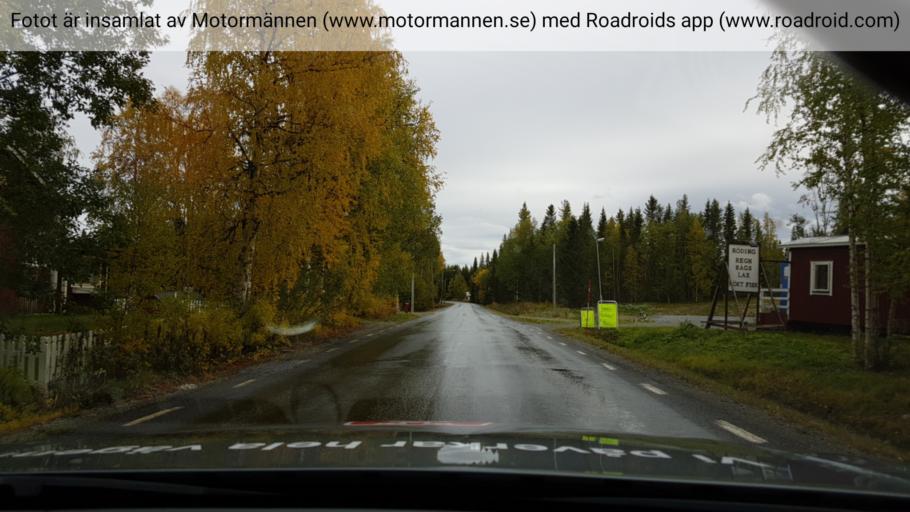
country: SE
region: Vaesterbotten
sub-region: Vilhelmina Kommun
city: Sjoberg
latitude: 64.6540
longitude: 16.3213
